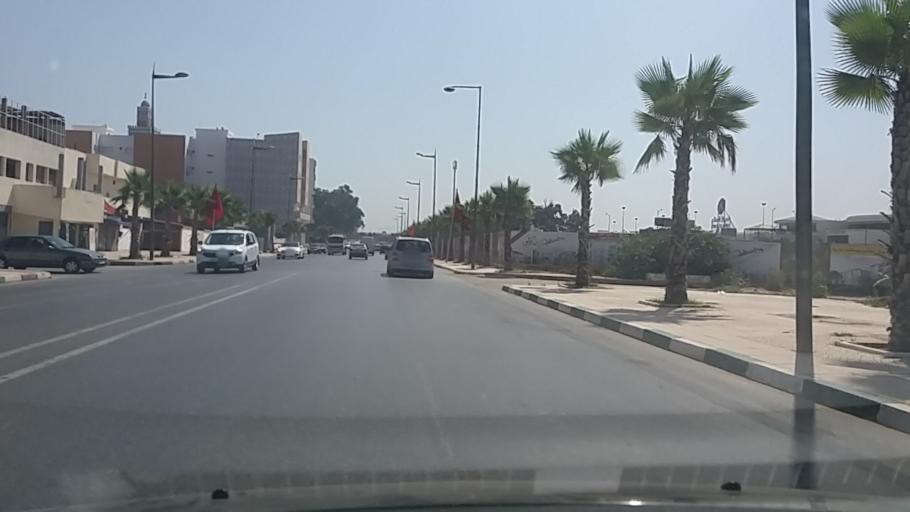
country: MA
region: Gharb-Chrarda-Beni Hssen
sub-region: Kenitra Province
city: Kenitra
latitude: 34.2488
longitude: -6.6120
